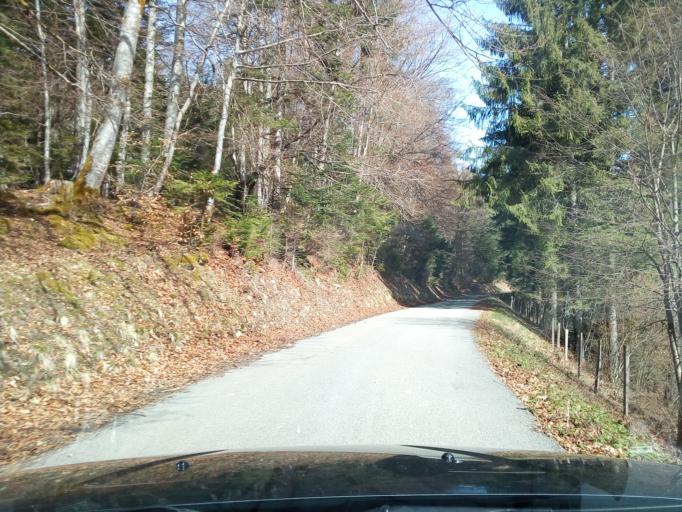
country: FR
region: Rhone-Alpes
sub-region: Departement de l'Isere
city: Revel
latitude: 45.1619
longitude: 5.8777
